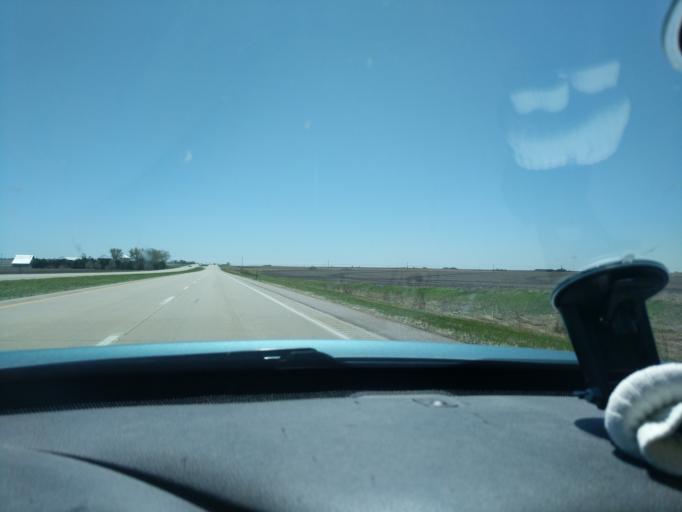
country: US
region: Nebraska
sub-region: Fillmore County
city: Geneva
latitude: 40.3695
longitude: -97.5774
